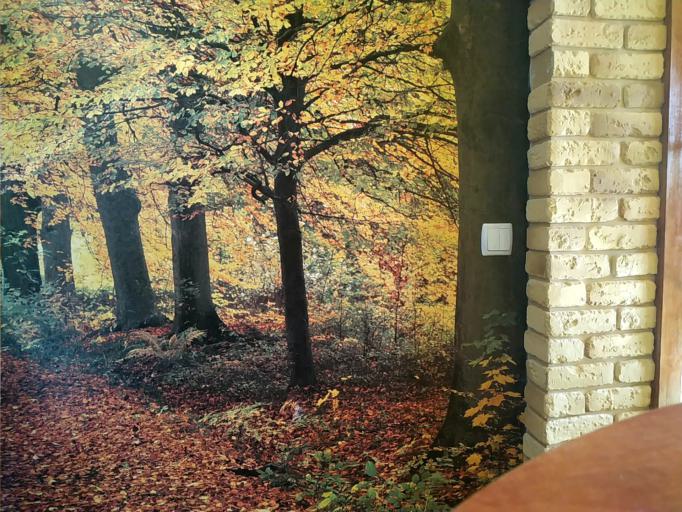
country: RU
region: Jaroslavl
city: Kukoboy
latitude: 58.8570
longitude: 39.7321
